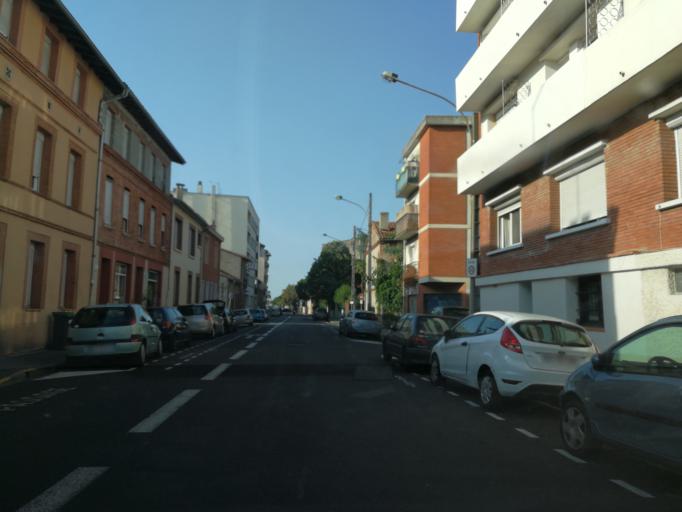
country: FR
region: Midi-Pyrenees
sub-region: Departement de la Haute-Garonne
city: Toulouse
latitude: 43.6196
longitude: 1.4371
